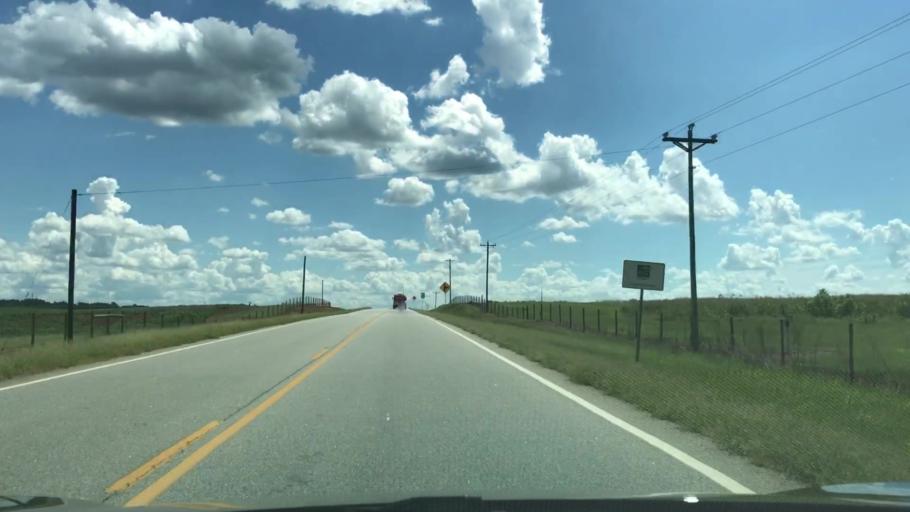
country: US
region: Georgia
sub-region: Oconee County
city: Watkinsville
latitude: 33.7292
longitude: -83.3026
